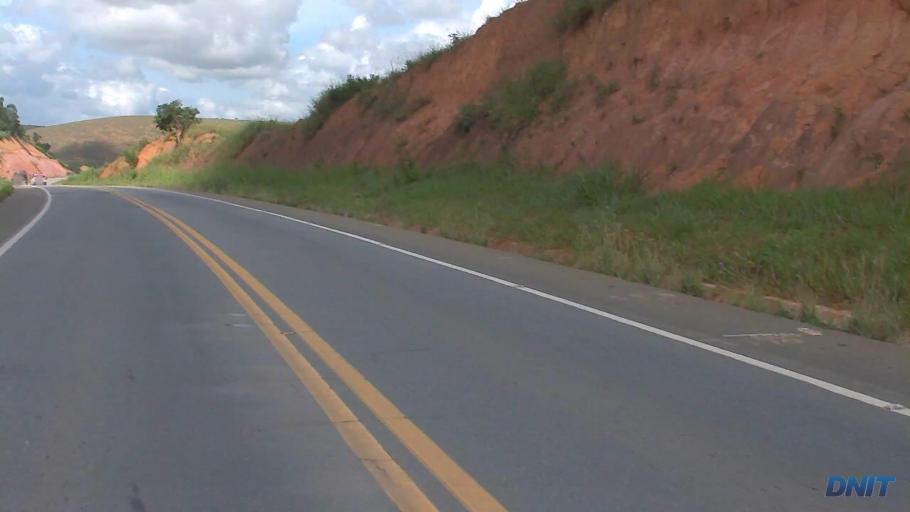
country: BR
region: Minas Gerais
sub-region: Belo Oriente
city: Belo Oriente
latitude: -19.1017
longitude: -42.1997
